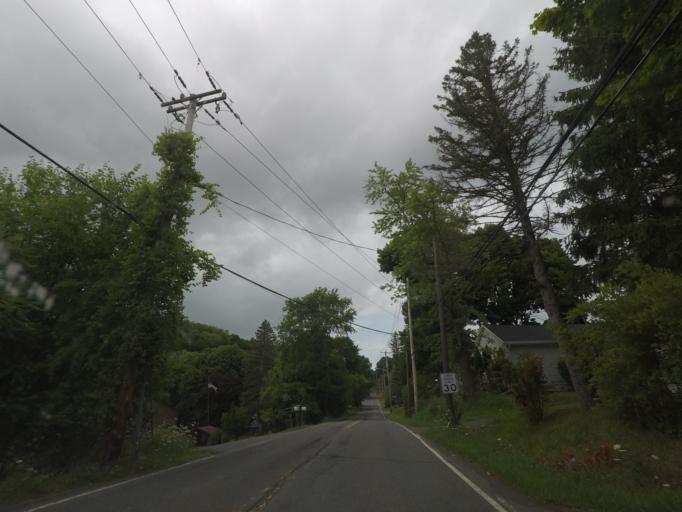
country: US
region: New York
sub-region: Rensselaer County
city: Wynantskill
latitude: 42.6660
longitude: -73.6363
